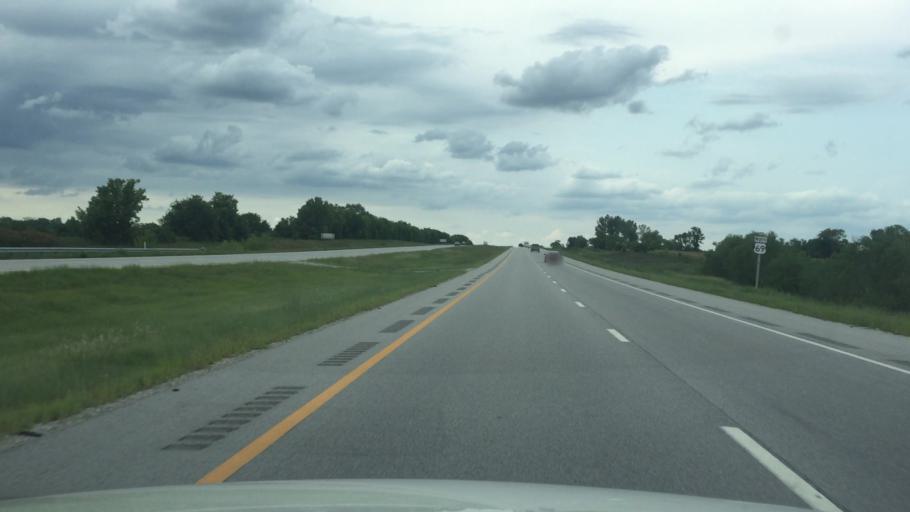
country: US
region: Kansas
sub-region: Miami County
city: Louisburg
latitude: 38.7280
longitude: -94.6764
